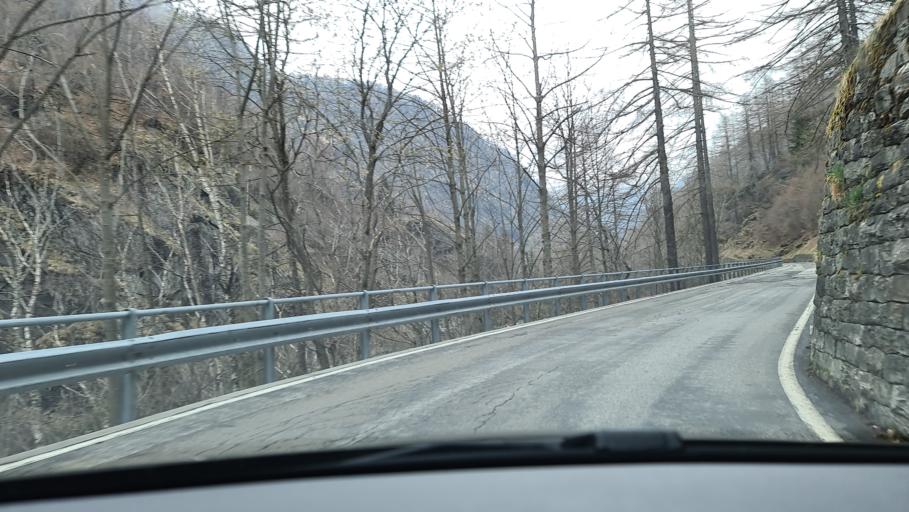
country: CH
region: Ticino
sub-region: Vallemaggia District
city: Cevio
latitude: 46.4191
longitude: 8.6523
